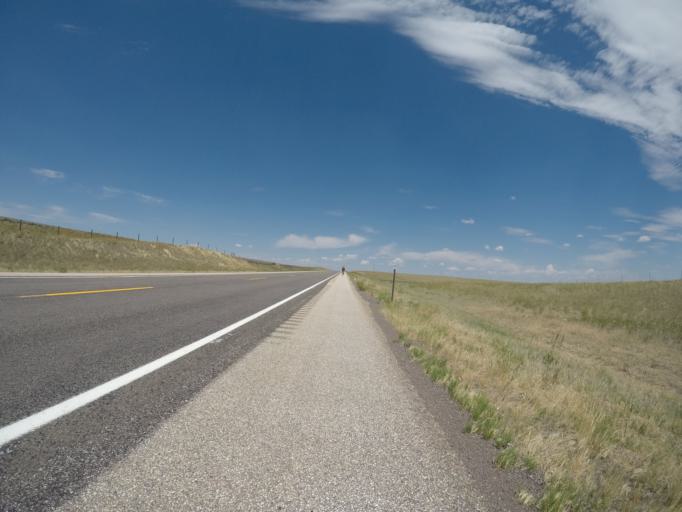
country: US
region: Wyoming
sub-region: Albany County
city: Laramie
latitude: 41.5618
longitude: -105.6874
